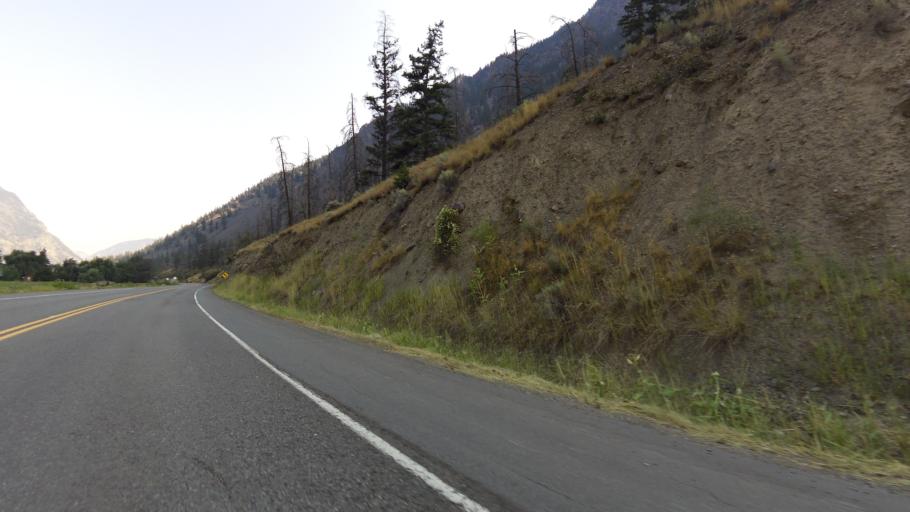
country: CA
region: British Columbia
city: Oliver
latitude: 49.2674
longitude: -120.0189
